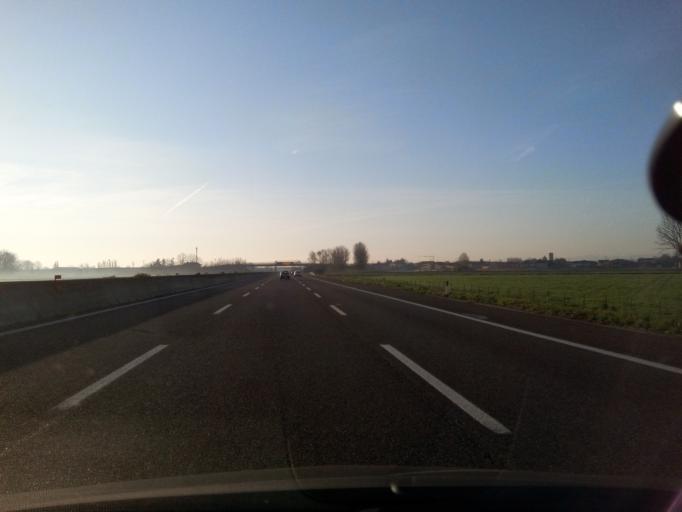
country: IT
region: Lombardy
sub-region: Provincia di Lodi
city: Guardamiglio
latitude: 45.1195
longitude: 9.6740
